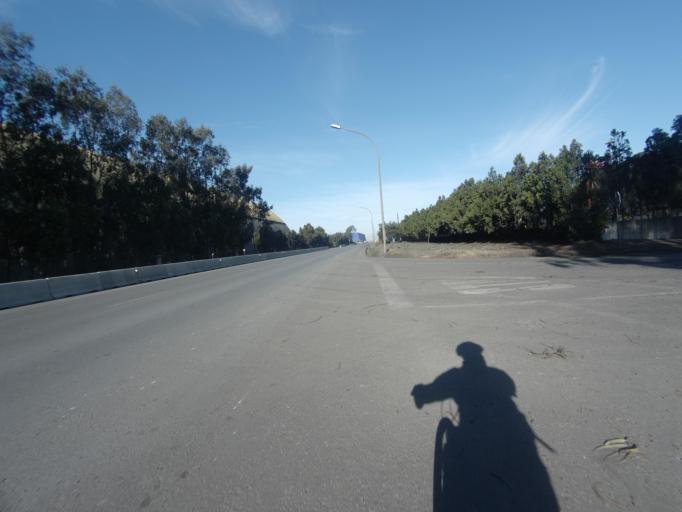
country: ES
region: Andalusia
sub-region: Provincia de Huelva
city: Punta Umbria
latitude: 37.1849
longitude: -6.9254
